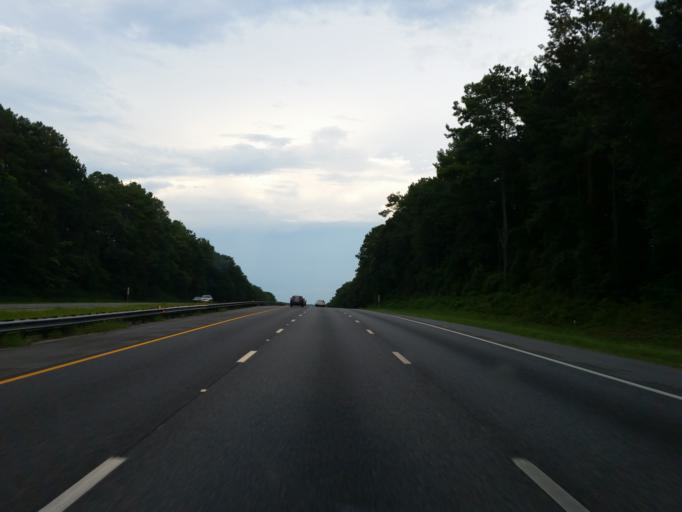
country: US
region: Florida
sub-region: Hamilton County
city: Jasper
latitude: 30.4937
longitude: -83.0319
